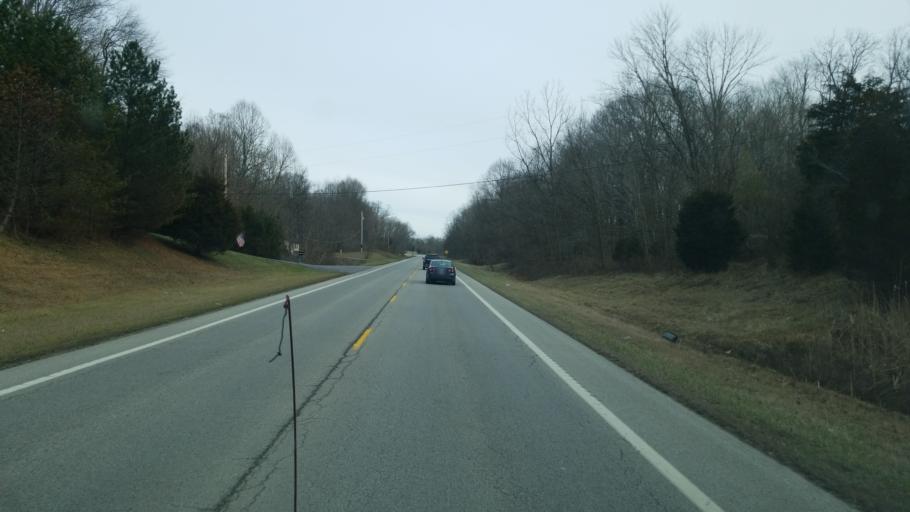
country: US
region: Ohio
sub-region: Highland County
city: Hillsboro
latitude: 39.1621
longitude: -83.6441
